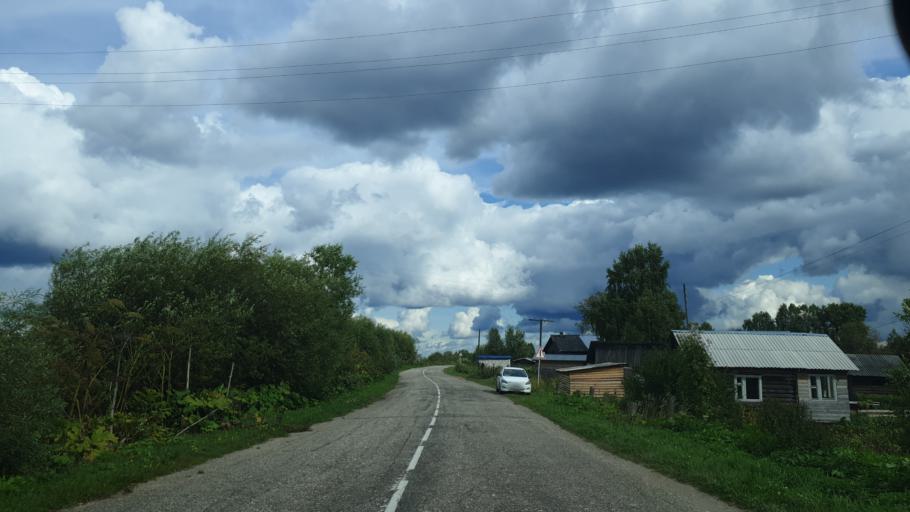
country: RU
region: Komi Republic
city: Aykino
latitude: 61.9539
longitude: 50.1778
